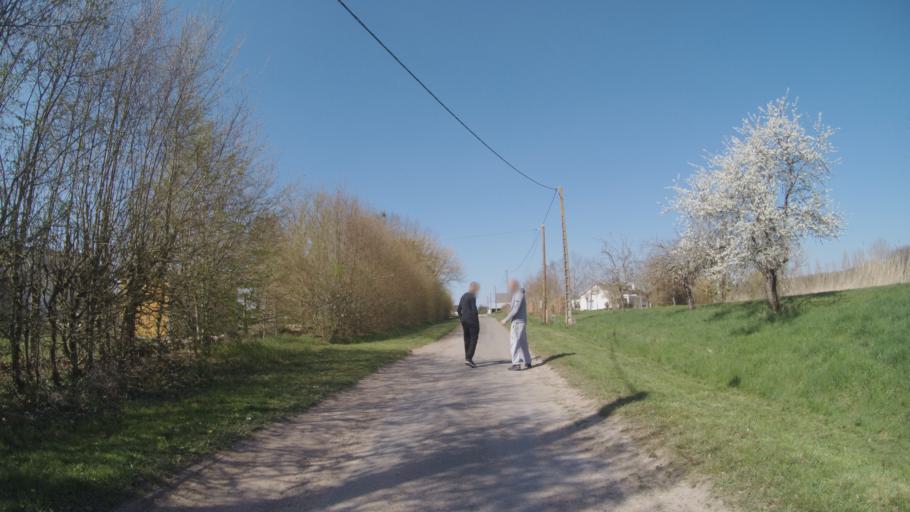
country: FR
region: Centre
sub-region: Departement du Loiret
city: Chanteau
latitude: 47.9617
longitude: 1.9751
